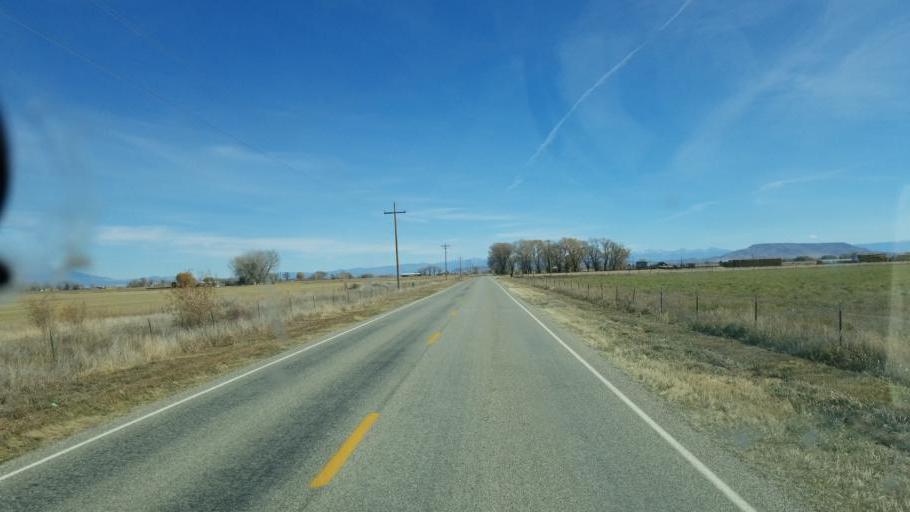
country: US
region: Colorado
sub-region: Conejos County
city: Conejos
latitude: 37.2837
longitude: -106.0334
